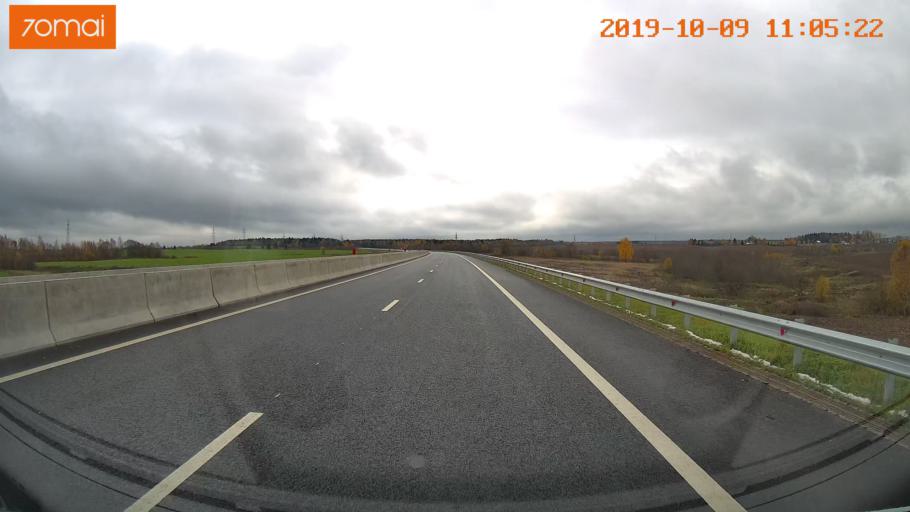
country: RU
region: Vologda
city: Molochnoye
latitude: 59.2012
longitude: 39.7592
